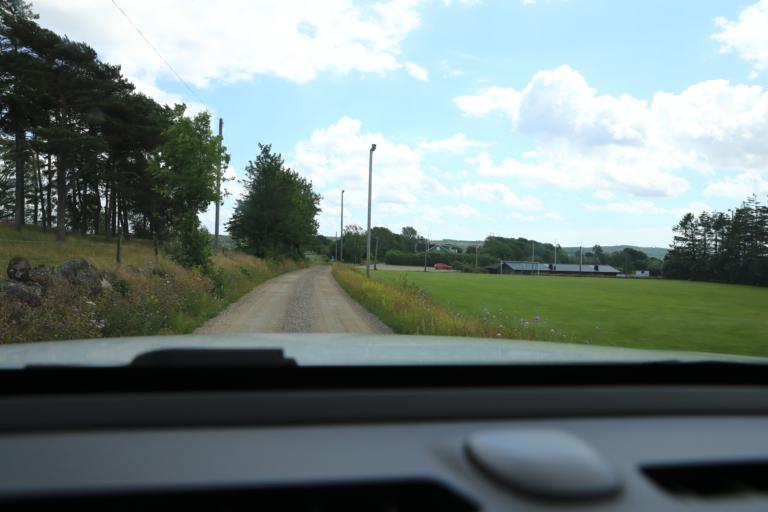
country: SE
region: Halland
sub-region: Varbergs Kommun
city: Tvaaker
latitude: 57.1103
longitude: 12.4116
